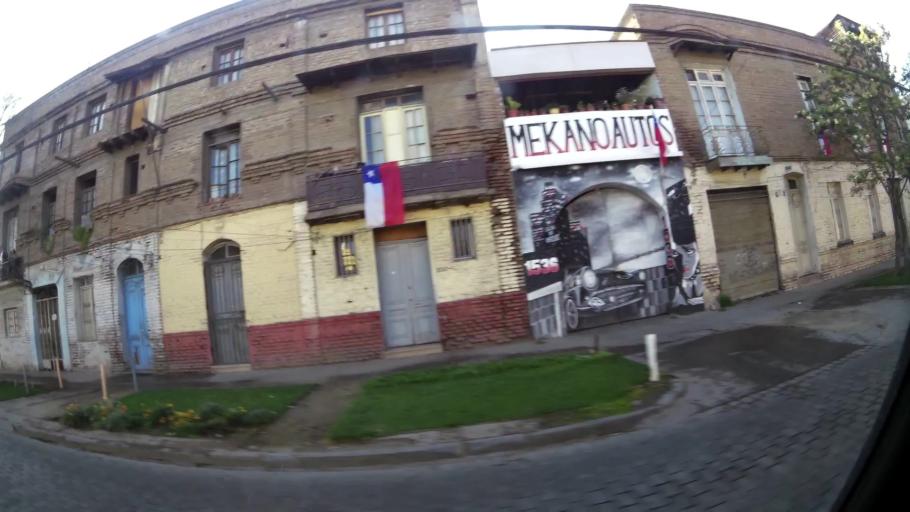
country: CL
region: Santiago Metropolitan
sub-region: Provincia de Santiago
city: Santiago
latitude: -33.4642
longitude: -70.6312
